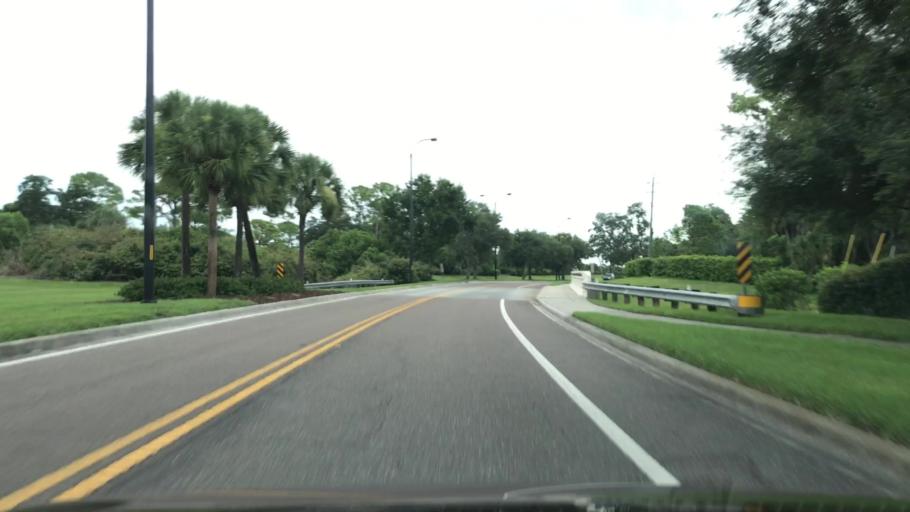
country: US
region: Florida
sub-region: Sarasota County
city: Vamo
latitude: 27.2370
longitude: -82.4814
